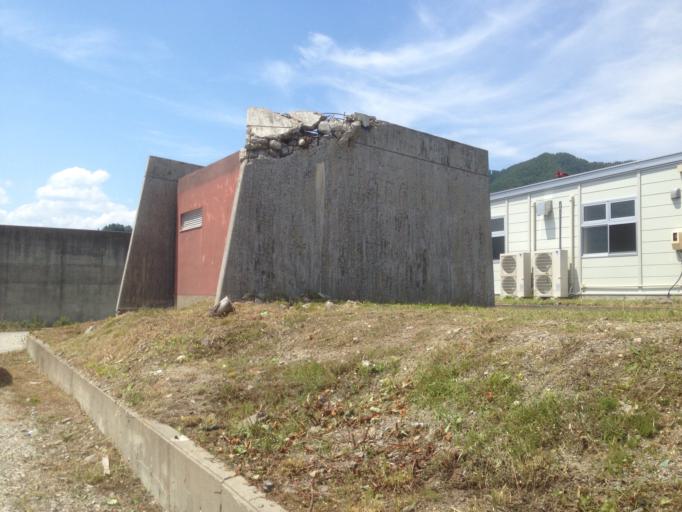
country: JP
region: Iwate
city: Otsuchi
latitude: 39.3512
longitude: 141.9340
